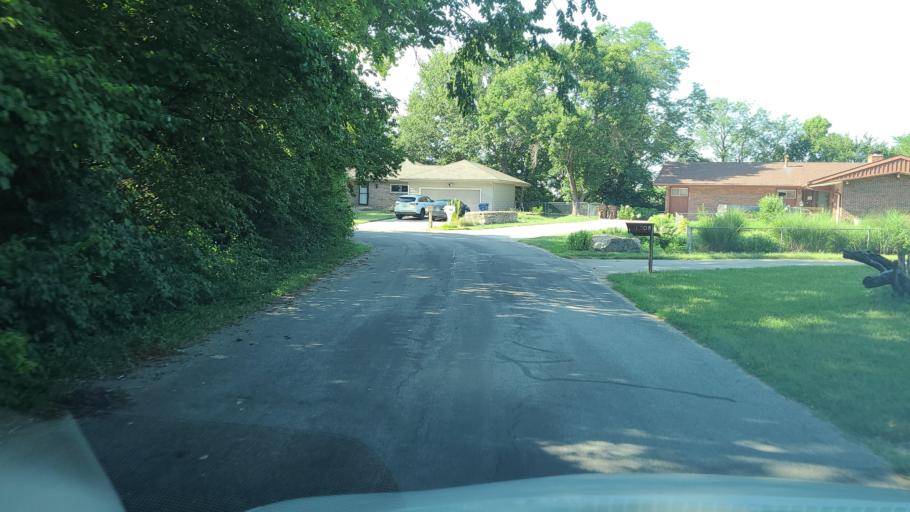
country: US
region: Kansas
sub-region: Douglas County
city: Lawrence
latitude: 38.9753
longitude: -95.2581
